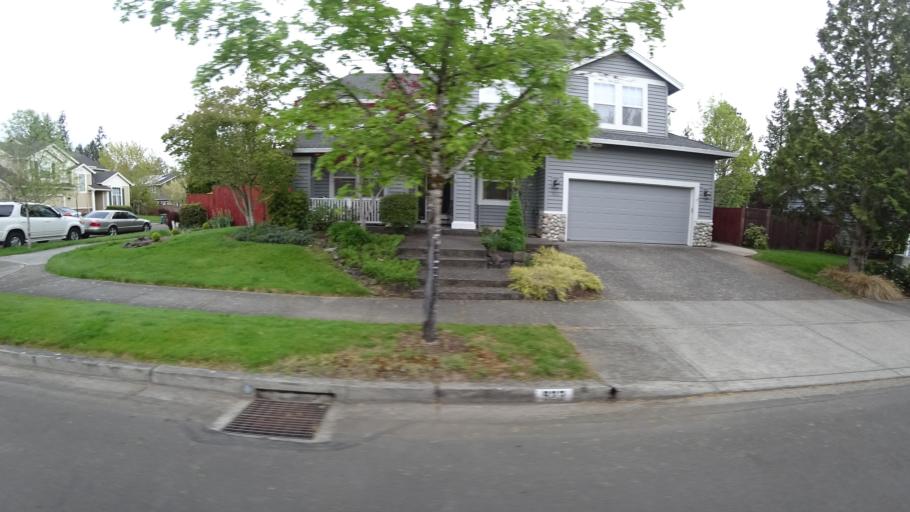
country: US
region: Oregon
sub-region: Washington County
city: Hillsboro
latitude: 45.5453
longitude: -122.9738
